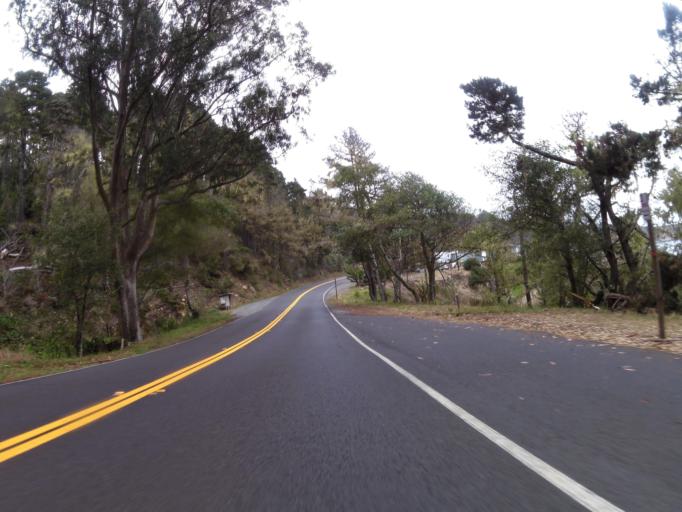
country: US
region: California
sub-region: Sonoma County
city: Sea Ranch
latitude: 38.5336
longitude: -123.2741
